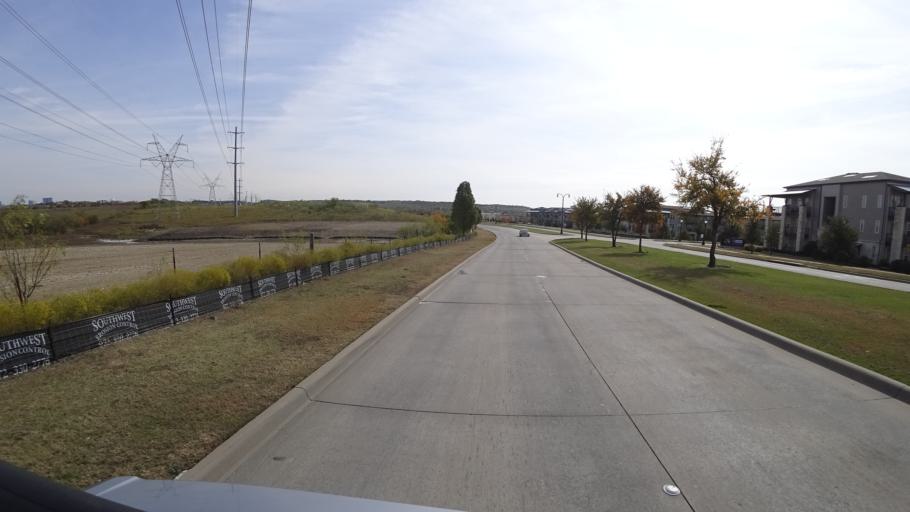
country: US
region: Texas
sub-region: Denton County
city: The Colony
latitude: 33.0601
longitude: -96.8677
